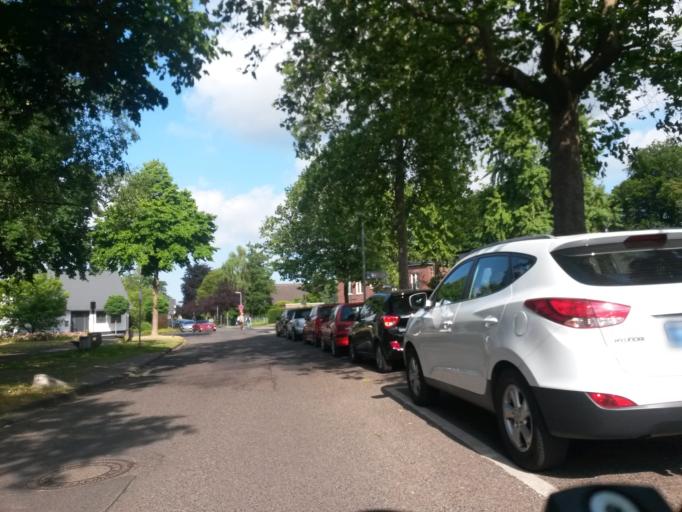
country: DE
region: North Rhine-Westphalia
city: Kempen
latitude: 51.3639
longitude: 6.4121
